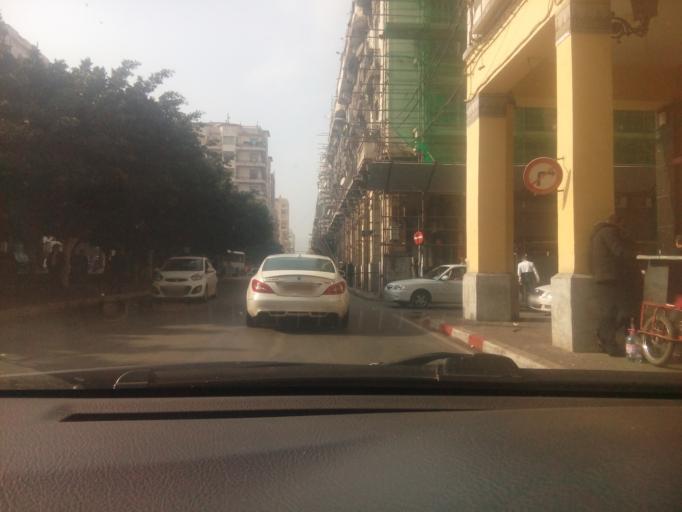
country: DZ
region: Oran
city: Oran
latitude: 35.7031
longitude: -0.6366
